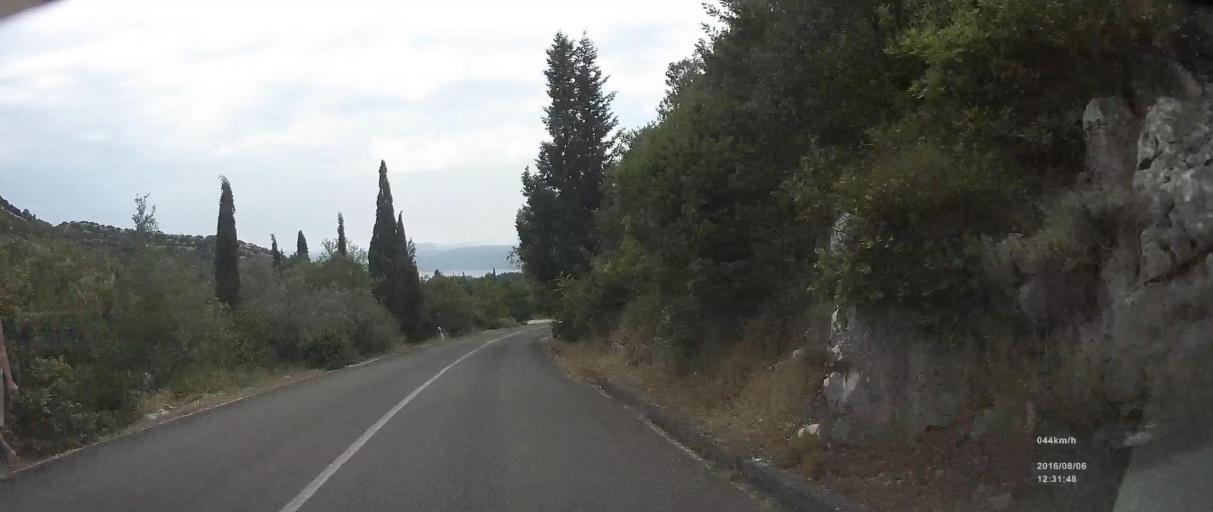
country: HR
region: Dubrovacko-Neretvanska
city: Ston
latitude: 42.7097
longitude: 17.7073
